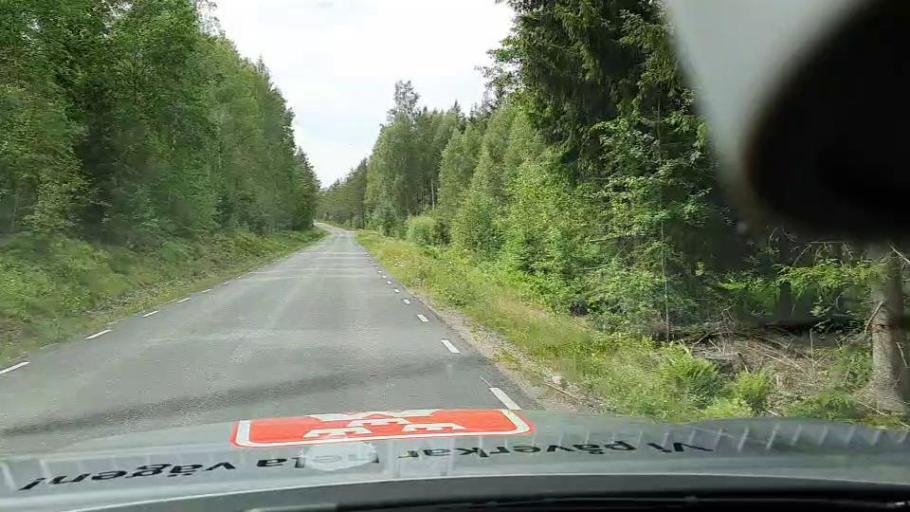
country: SE
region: Soedermanland
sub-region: Eskilstuna Kommun
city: Arla
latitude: 59.2315
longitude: 16.7401
